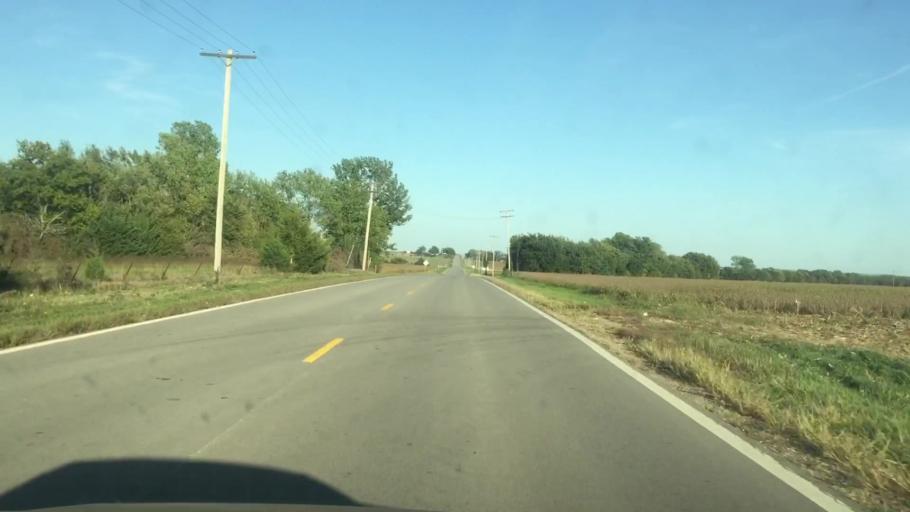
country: US
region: Kansas
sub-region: Brown County
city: Horton
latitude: 39.5876
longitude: -95.6076
